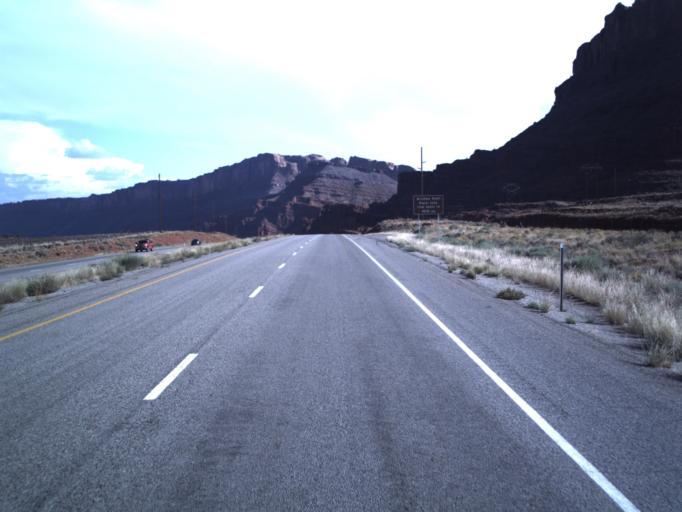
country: US
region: Utah
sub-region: Grand County
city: Moab
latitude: 38.6469
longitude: -109.6712
